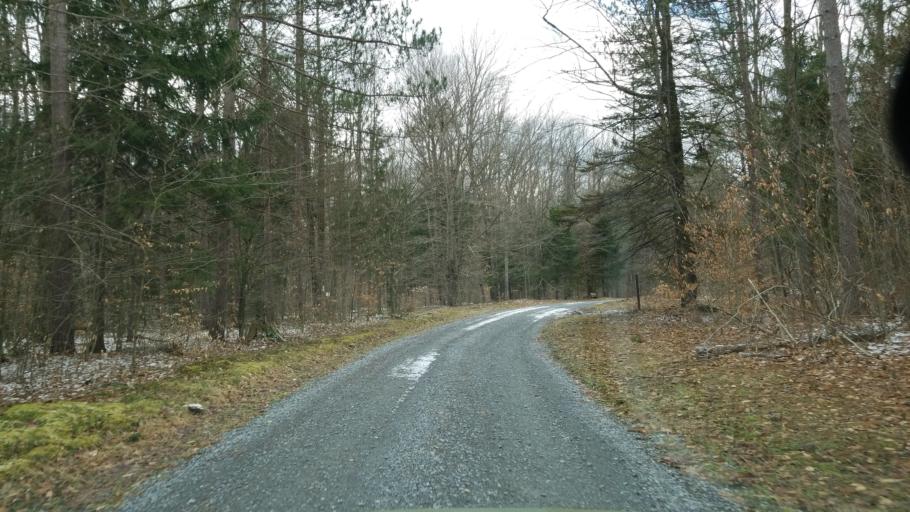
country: US
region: Pennsylvania
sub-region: Clearfield County
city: Clearfield
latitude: 41.1396
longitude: -78.5353
